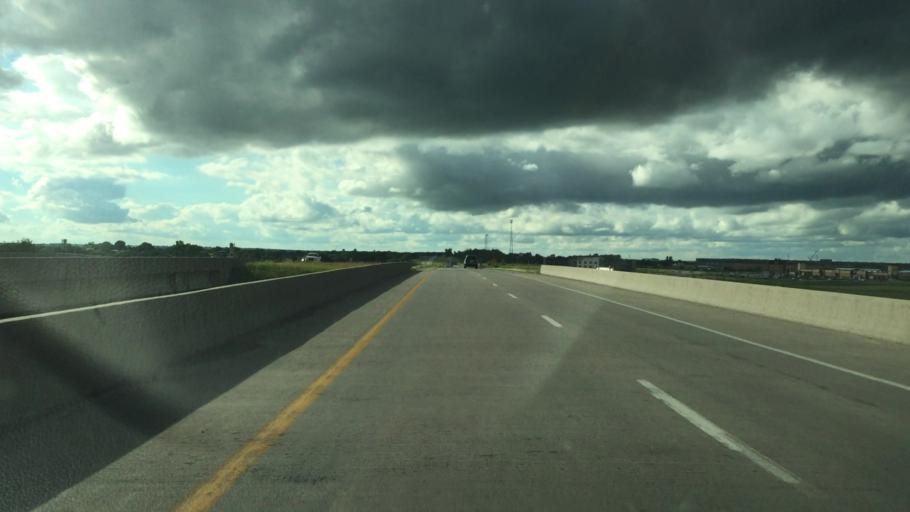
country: US
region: Iowa
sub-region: Polk County
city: Altoona
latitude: 41.6473
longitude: -93.5124
